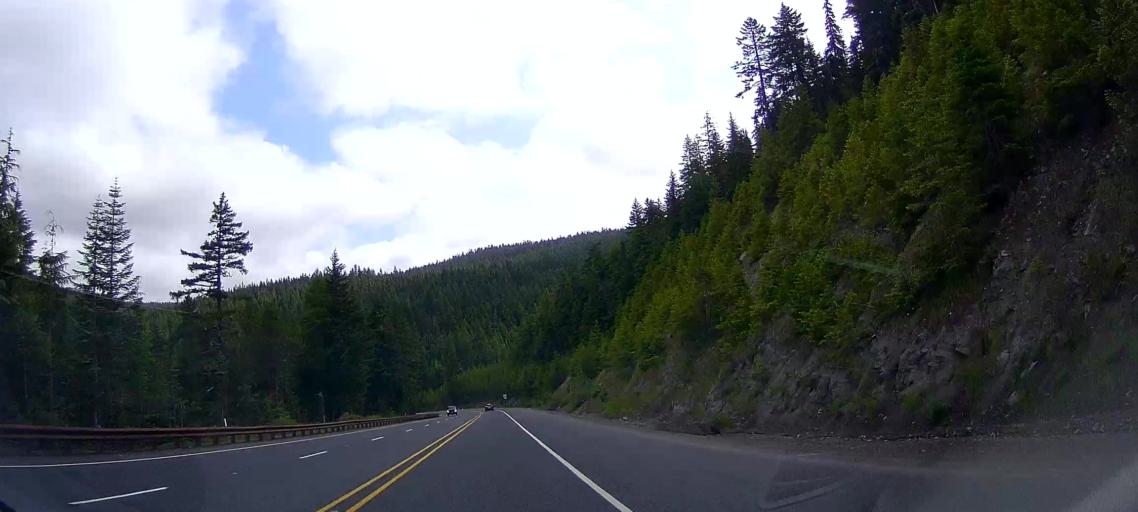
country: US
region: Oregon
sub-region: Clackamas County
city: Mount Hood Village
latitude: 45.2343
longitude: -121.7002
